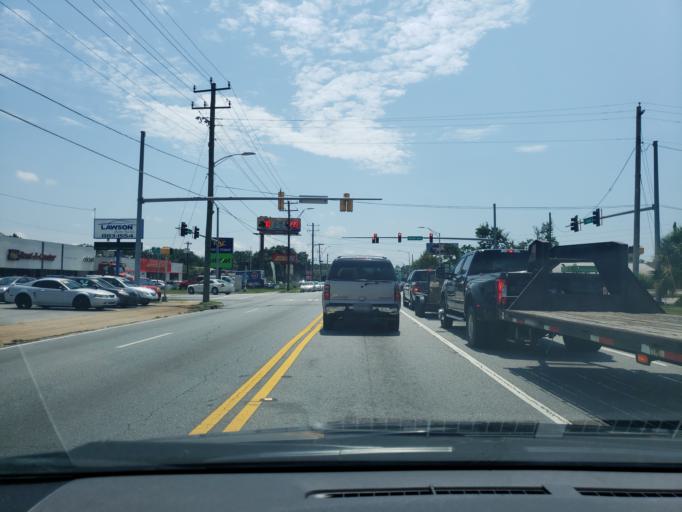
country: US
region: Georgia
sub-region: Dougherty County
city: Albany
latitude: 31.5772
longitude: -84.1762
